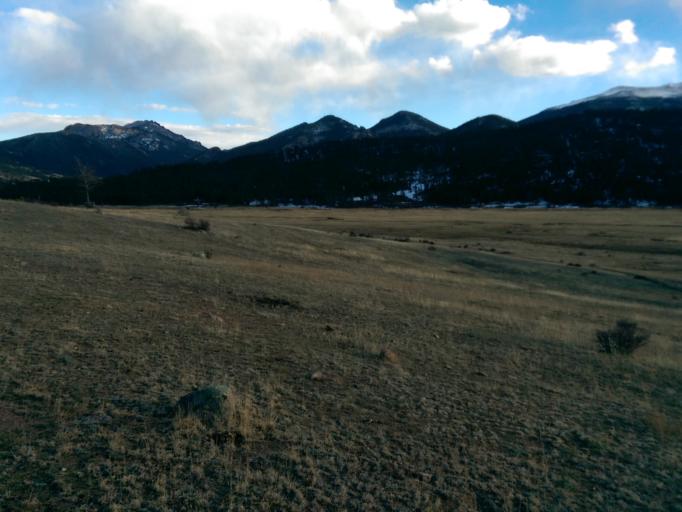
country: US
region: Colorado
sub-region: Larimer County
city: Estes Park
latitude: 40.3584
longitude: -105.5934
